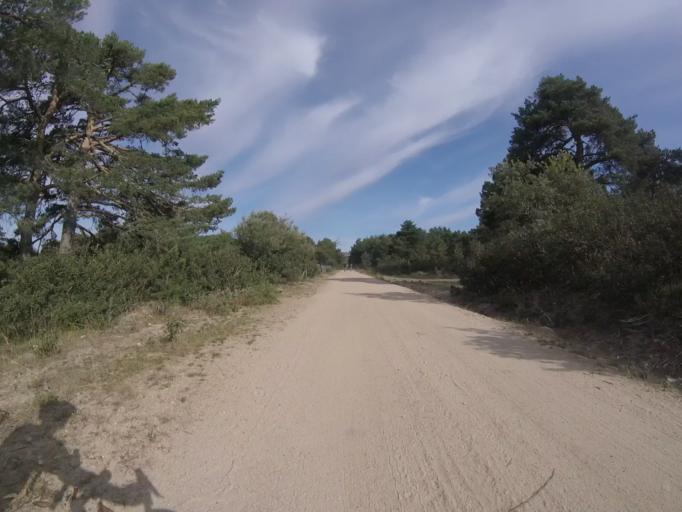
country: ES
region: Castille and Leon
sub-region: Provincia de Avila
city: Peguerinos
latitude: 40.6509
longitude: -4.1787
